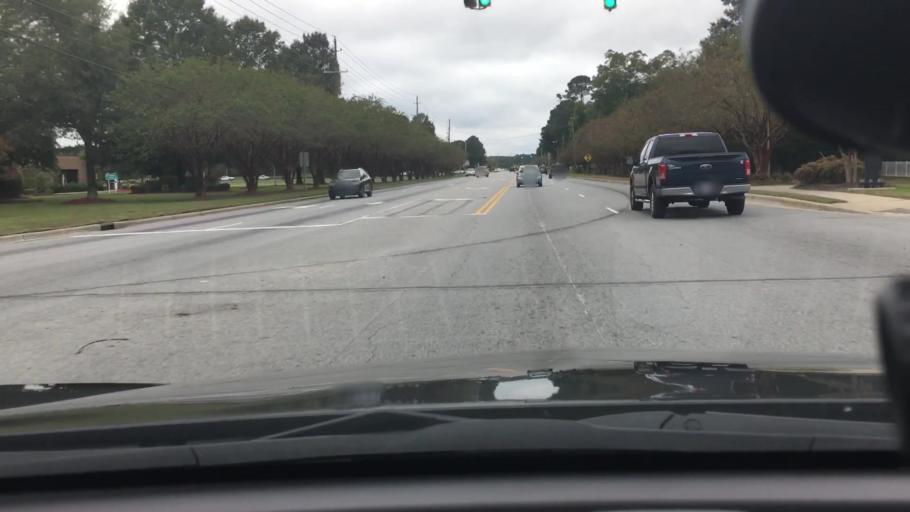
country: US
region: North Carolina
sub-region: Pitt County
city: Summerfield
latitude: 35.6063
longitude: -77.4174
